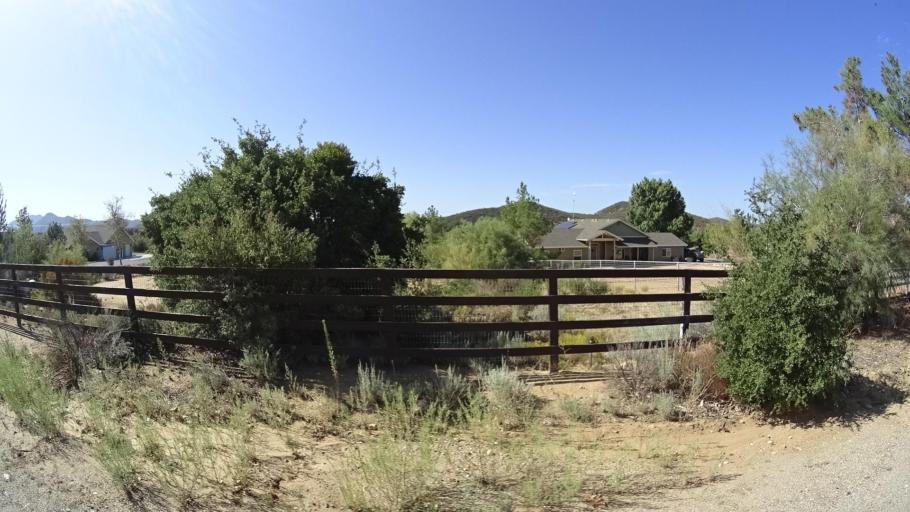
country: US
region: California
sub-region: Riverside County
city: Anza
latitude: 33.3859
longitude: -116.6634
